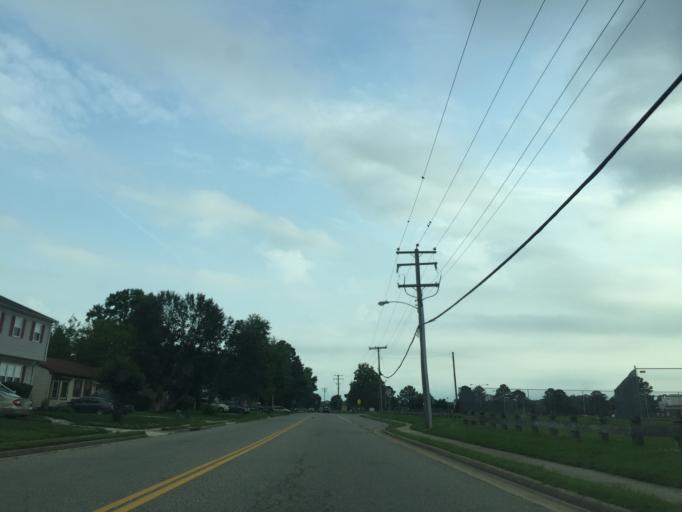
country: US
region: Virginia
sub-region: York County
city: Yorktown
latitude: 37.0979
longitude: -76.5271
